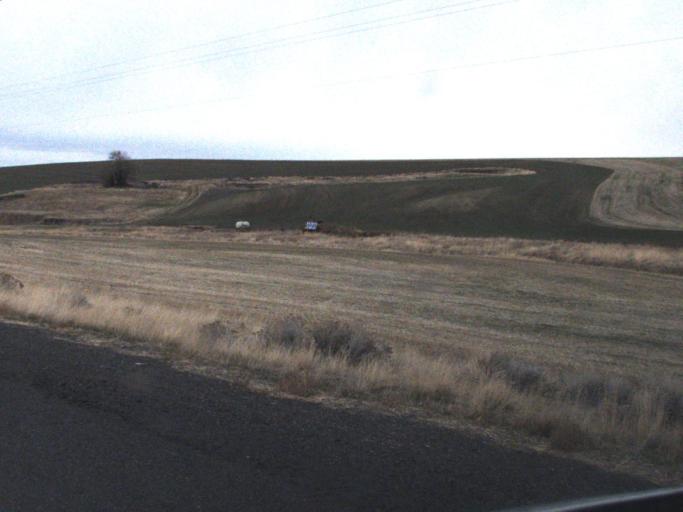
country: US
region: Washington
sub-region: Garfield County
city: Pomeroy
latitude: 46.8104
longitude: -117.8206
